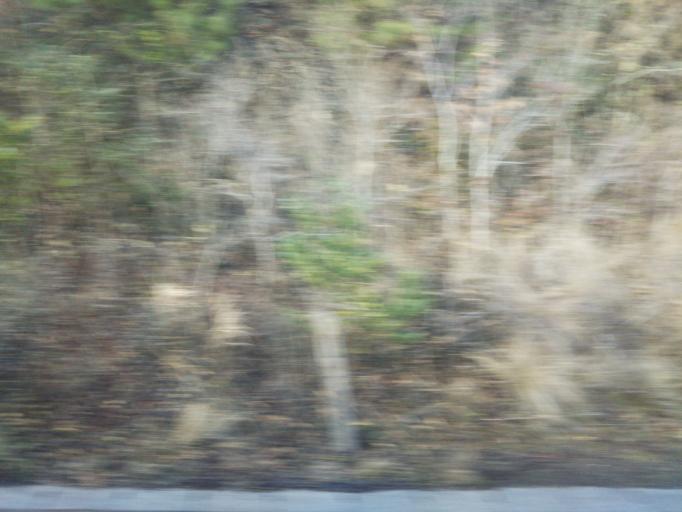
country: JP
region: Kagawa
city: Sakaidecho
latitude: 34.4542
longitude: 133.8071
